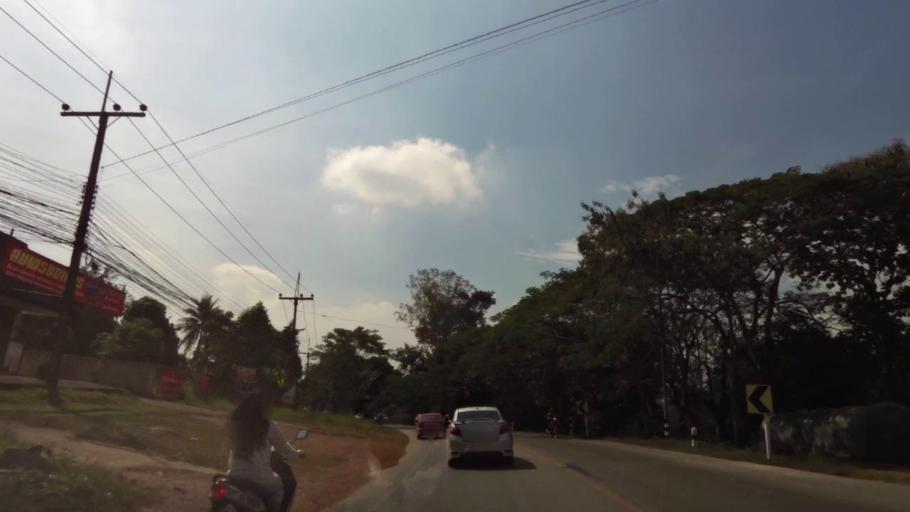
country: TH
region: Chiang Rai
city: Chiang Rai
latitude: 19.8751
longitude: 99.7826
